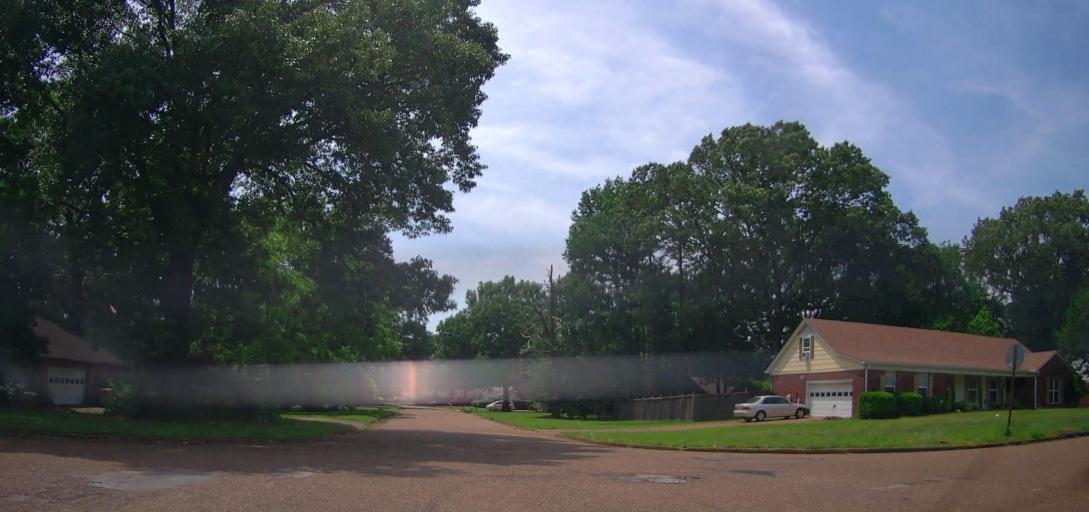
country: US
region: Tennessee
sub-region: Shelby County
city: Germantown
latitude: 35.0440
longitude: -89.7892
